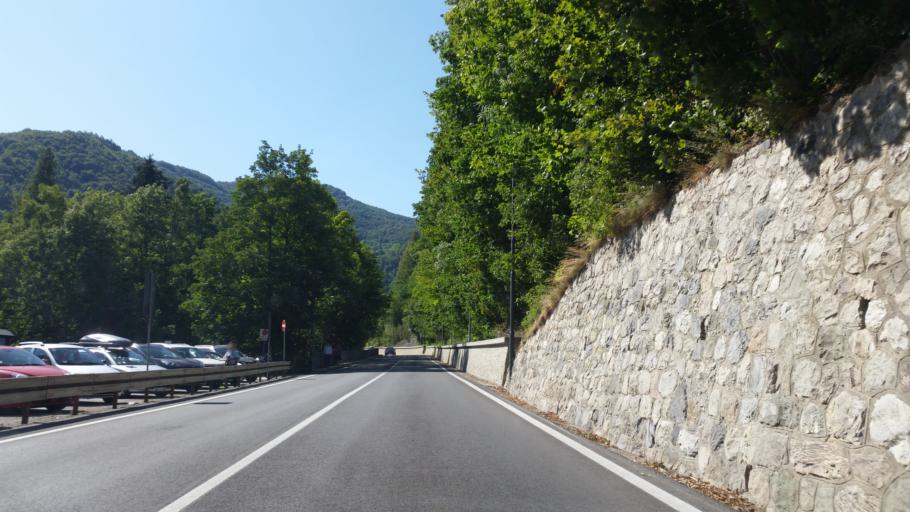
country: IT
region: Piedmont
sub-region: Provincia di Cuneo
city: Limone Piemonte
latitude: 44.2018
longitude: 7.5744
